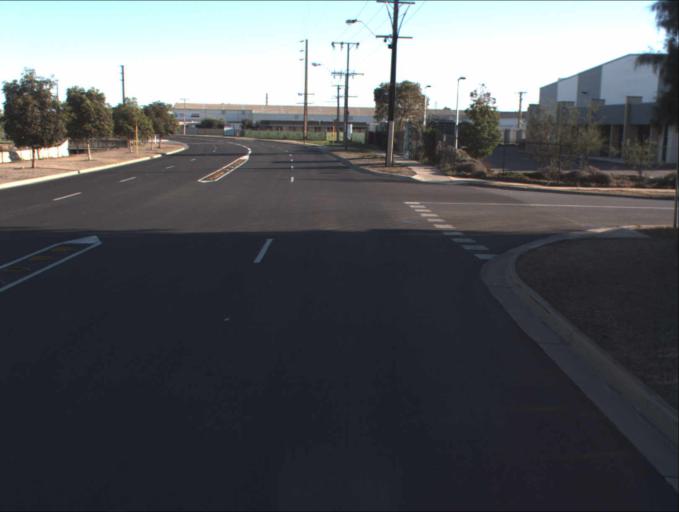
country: AU
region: South Australia
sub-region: Port Adelaide Enfield
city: Alberton
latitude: -34.8424
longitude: 138.5306
